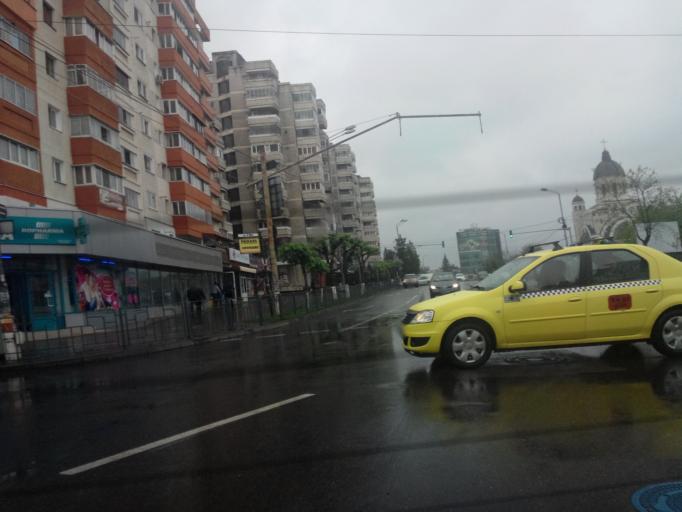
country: RO
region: Bacau
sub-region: Municipiul Bacau
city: Bacau
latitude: 46.5700
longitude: 26.9151
